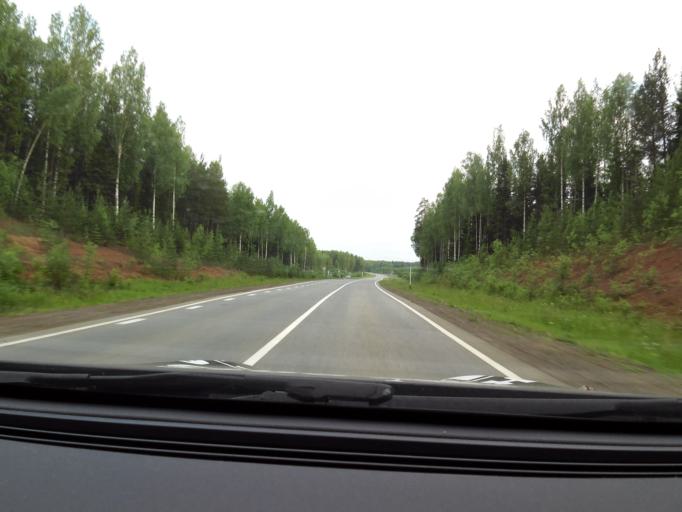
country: RU
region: Perm
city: Siva
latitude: 58.4437
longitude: 54.4292
